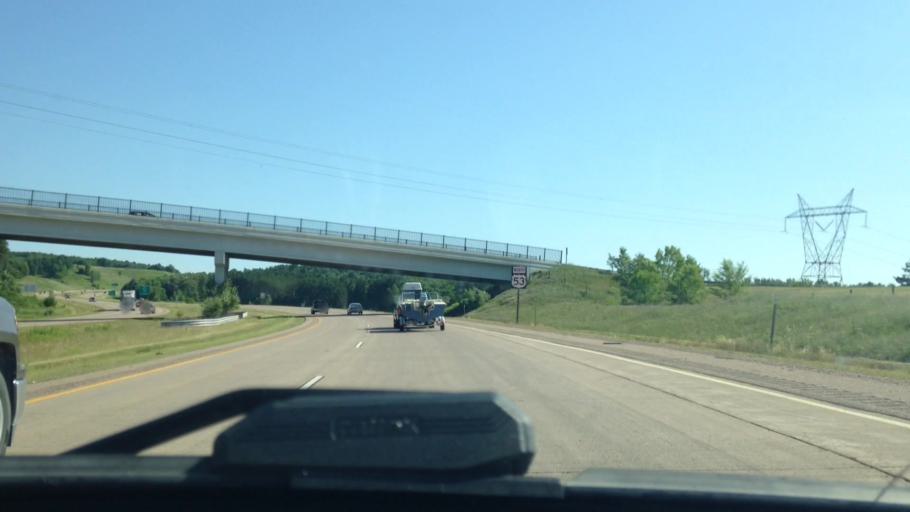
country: US
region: Wisconsin
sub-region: Eau Claire County
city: Seymour
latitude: 44.8389
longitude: -91.4415
